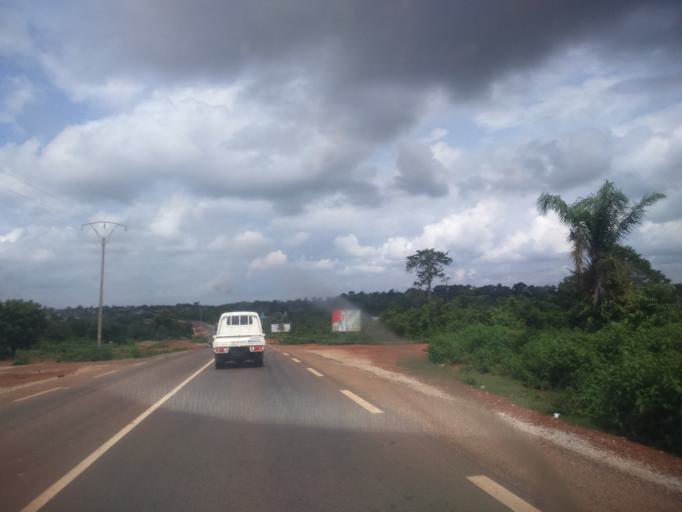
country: CI
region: Moyen-Comoe
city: Abengourou
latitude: 6.7217
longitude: -3.5271
